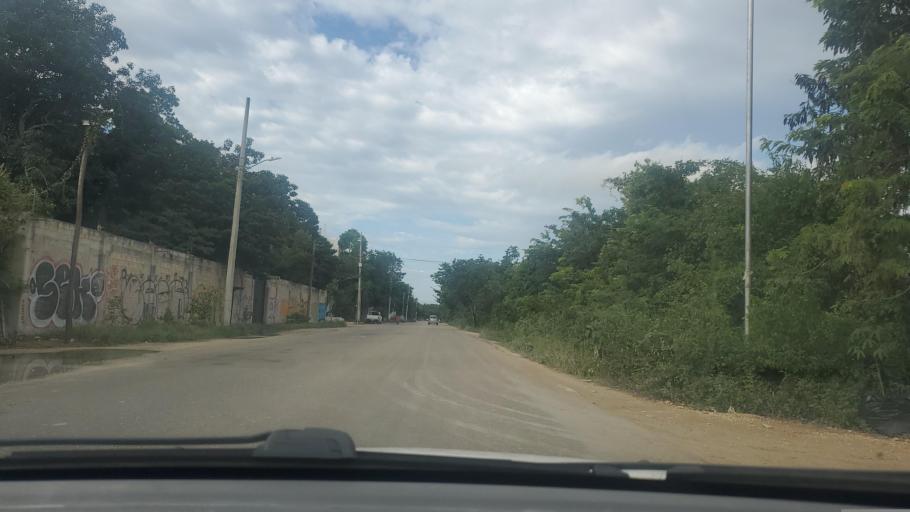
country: MX
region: Quintana Roo
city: Tulum
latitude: 20.2104
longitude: -87.4760
